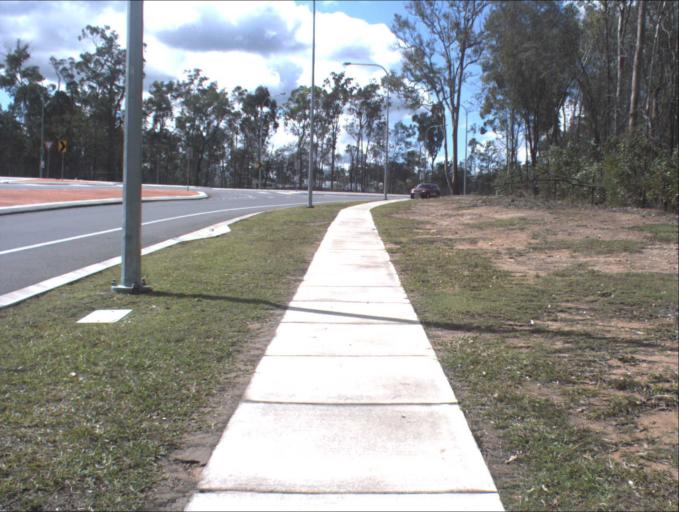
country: AU
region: Queensland
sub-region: Logan
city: Park Ridge South
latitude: -27.7059
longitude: 152.9746
